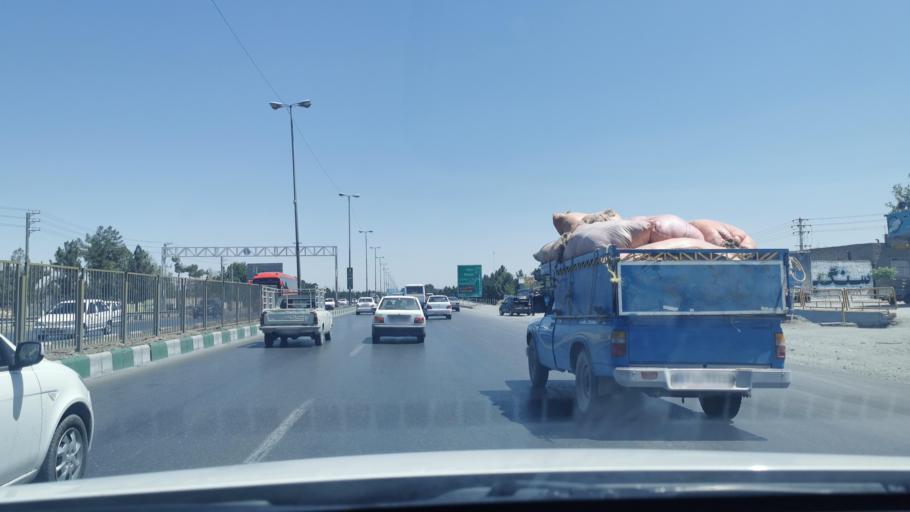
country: IR
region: Razavi Khorasan
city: Torqabeh
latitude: 36.4221
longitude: 59.4608
